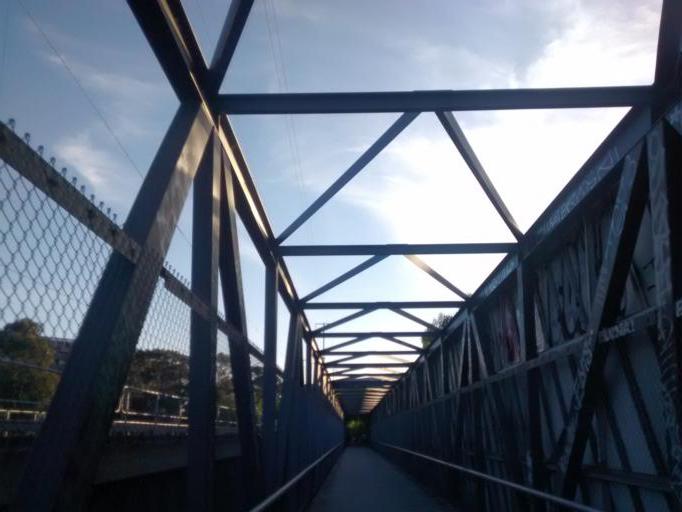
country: AU
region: Victoria
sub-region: Moonee Valley
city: Travancore
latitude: -37.7873
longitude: 144.9409
